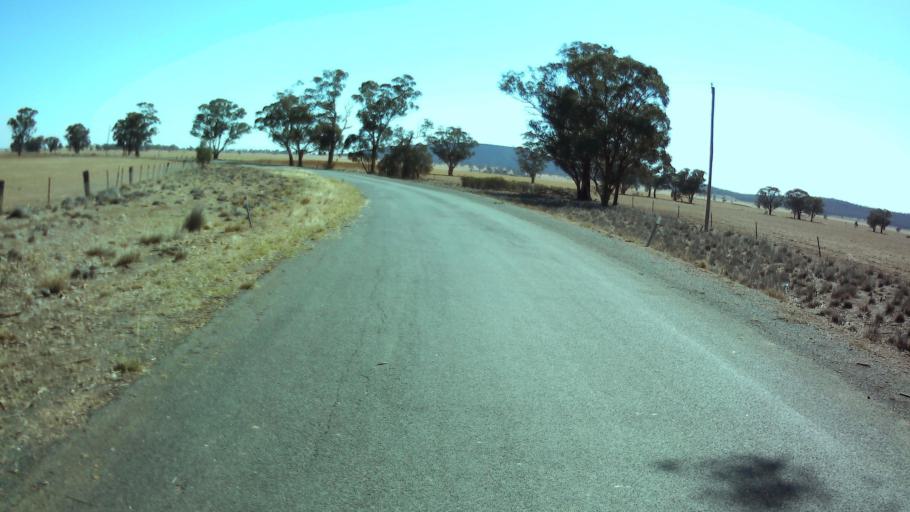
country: AU
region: New South Wales
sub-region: Weddin
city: Grenfell
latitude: -33.7057
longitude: 147.9175
